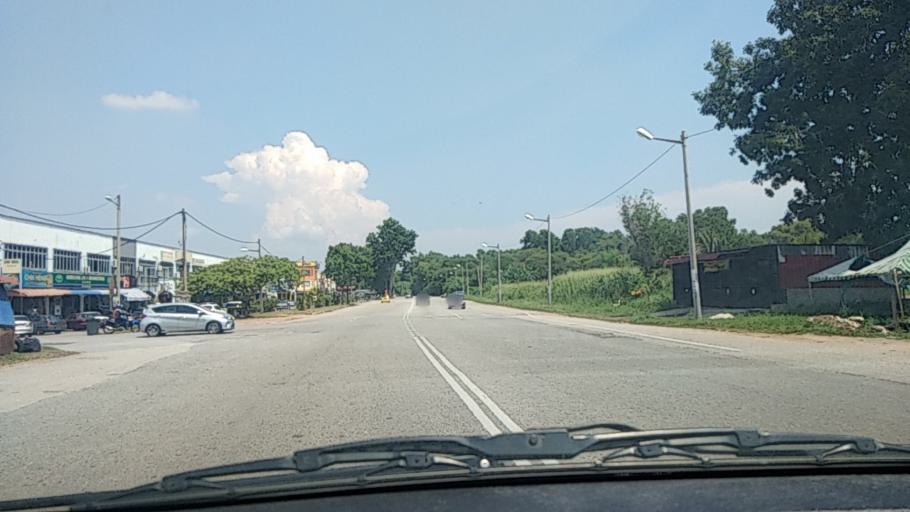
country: MY
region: Kedah
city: Sungai Petani
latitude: 5.6421
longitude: 100.5147
